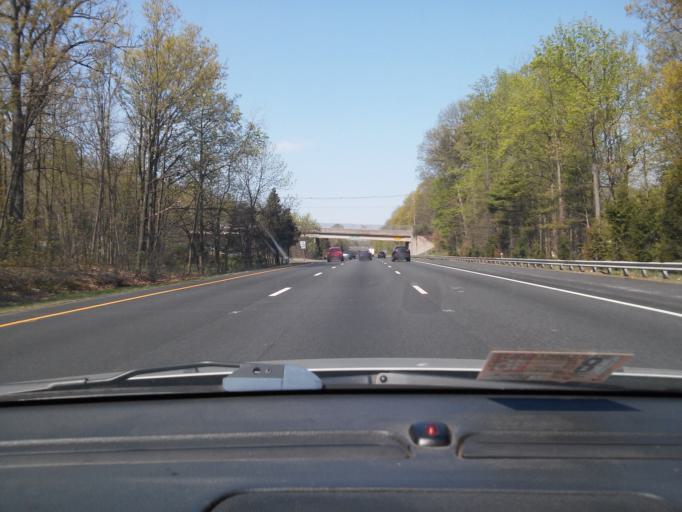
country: US
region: New Jersey
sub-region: Somerset County
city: Watchung
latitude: 40.6487
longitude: -74.4898
